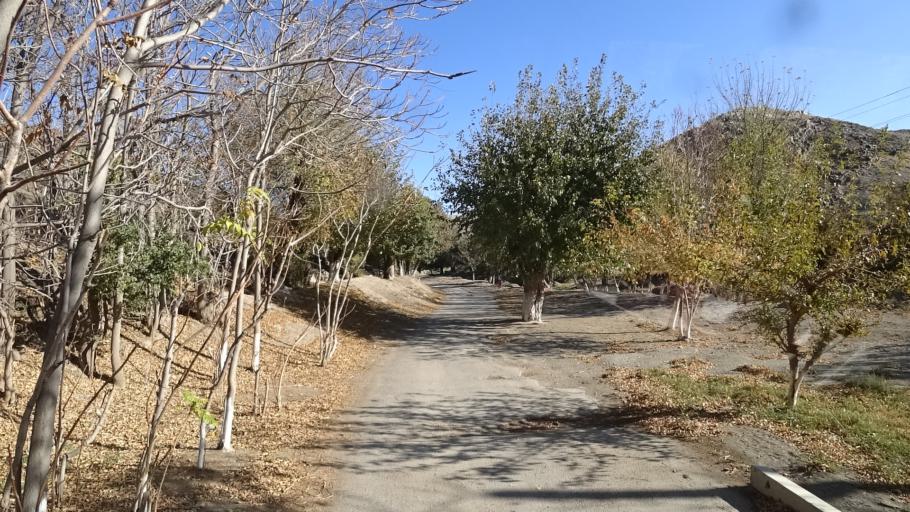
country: UZ
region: Navoiy
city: Karmana Shahri
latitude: 40.2956
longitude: 65.6044
